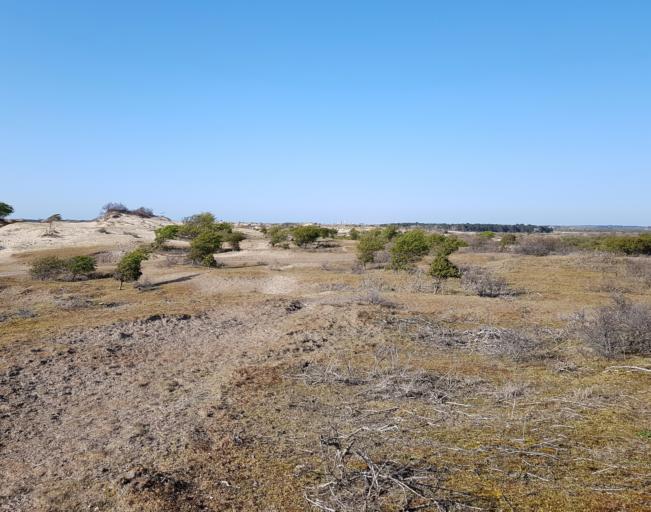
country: NL
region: South Holland
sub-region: Gemeente Noordwijkerhout
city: Noordwijkerhout
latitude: 52.3046
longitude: 4.5043
